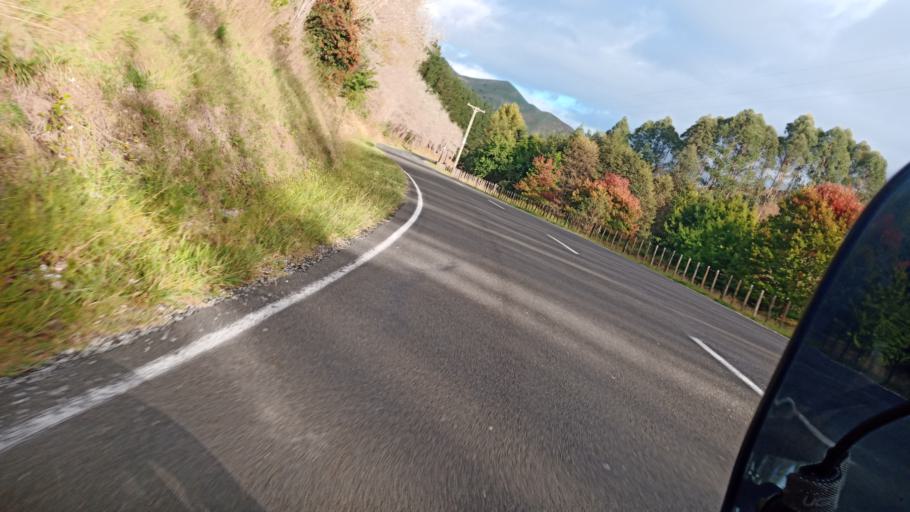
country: NZ
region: Gisborne
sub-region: Gisborne District
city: Gisborne
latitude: -38.5606
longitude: 177.7101
